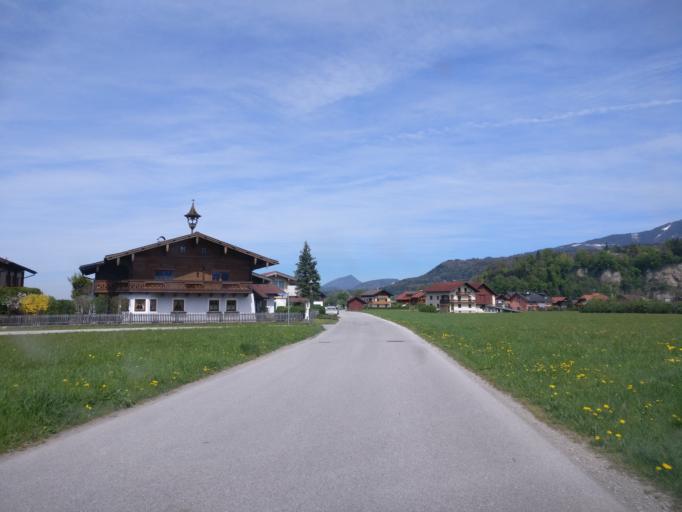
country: AT
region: Salzburg
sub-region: Politischer Bezirk Hallein
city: Kuchl
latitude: 47.6284
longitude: 13.1548
